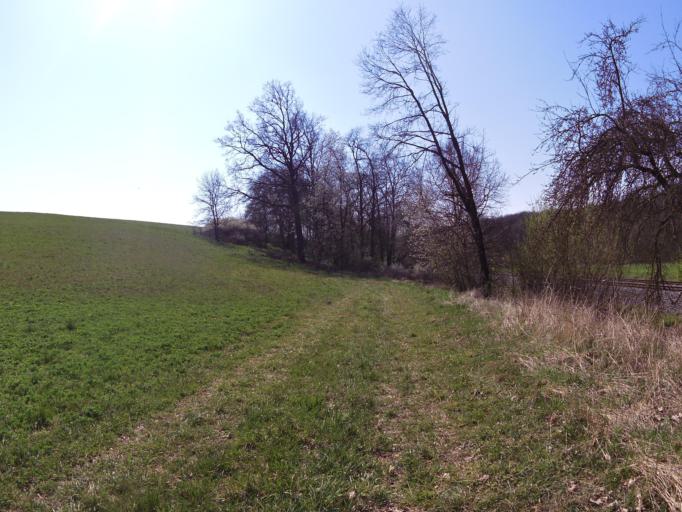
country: DE
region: Bavaria
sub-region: Regierungsbezirk Unterfranken
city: Rottendorf
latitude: 49.8207
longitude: 10.0690
